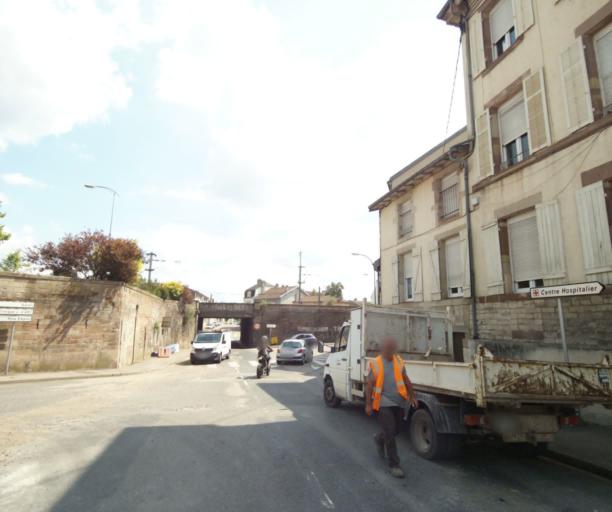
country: FR
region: Lorraine
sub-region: Departement de Meurthe-et-Moselle
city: Luneville
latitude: 48.5877
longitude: 6.4935
